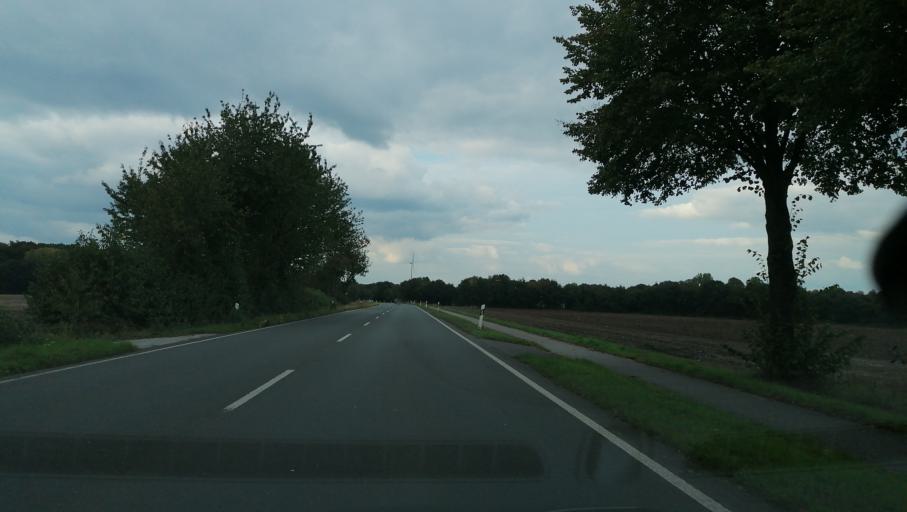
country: DE
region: North Rhine-Westphalia
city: Marl
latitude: 51.6148
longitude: 7.0488
